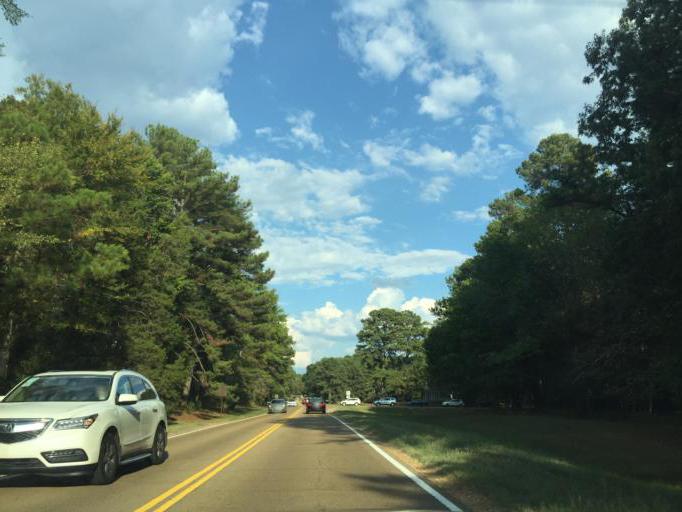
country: US
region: Mississippi
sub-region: Madison County
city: Ridgeland
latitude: 32.4264
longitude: -90.1279
